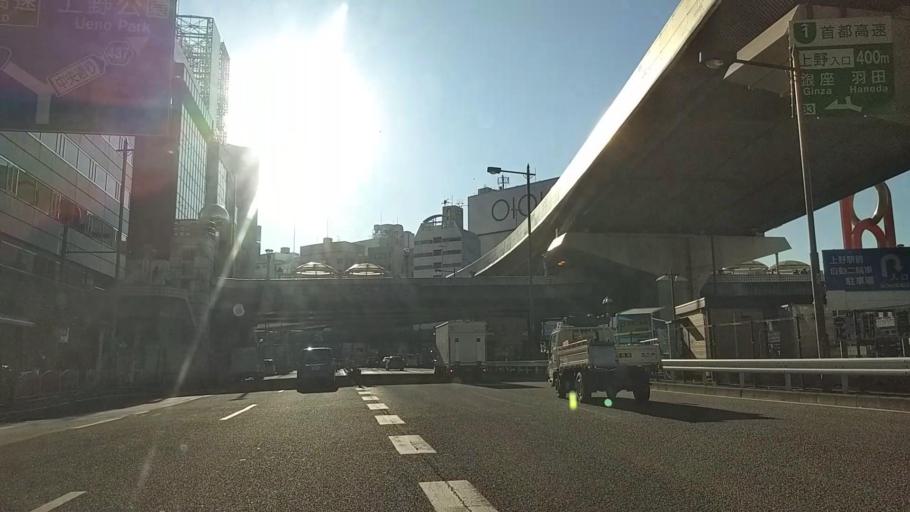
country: JP
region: Tokyo
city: Tokyo
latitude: 35.7120
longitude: 139.7781
